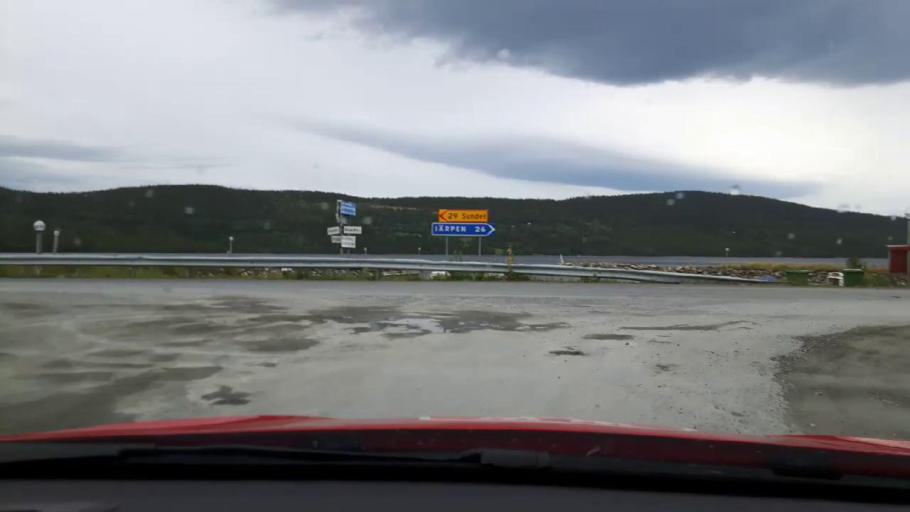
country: SE
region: Jaemtland
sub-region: Are Kommun
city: Are
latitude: 63.4940
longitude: 13.1232
